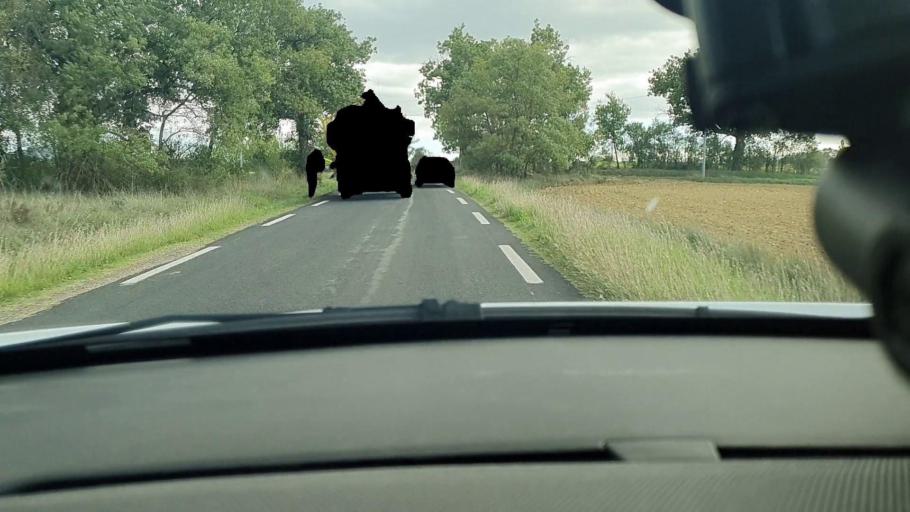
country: FR
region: Languedoc-Roussillon
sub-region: Departement du Gard
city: Les Mages
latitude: 44.1975
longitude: 4.2107
